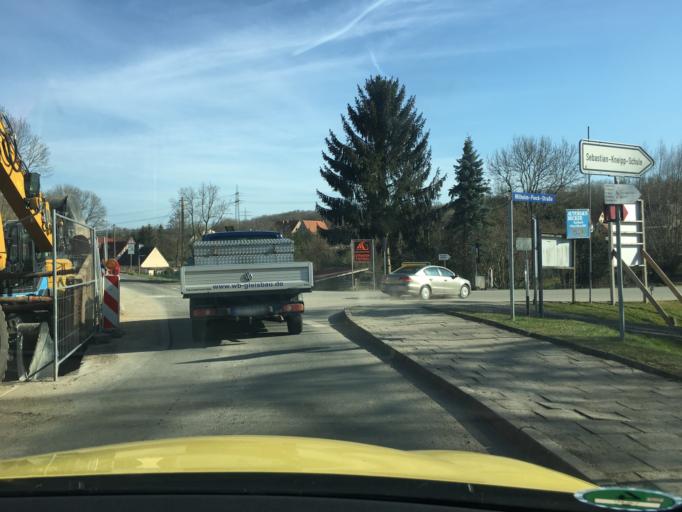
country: DE
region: Saxony-Anhalt
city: Bad Bibra
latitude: 51.2147
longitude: 11.5280
